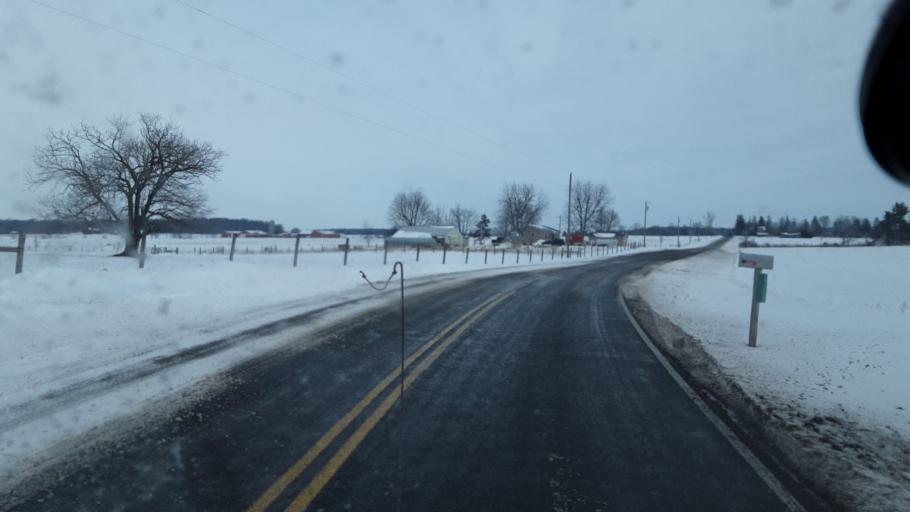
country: US
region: Ohio
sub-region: Union County
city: Marysville
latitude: 40.1879
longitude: -83.3651
